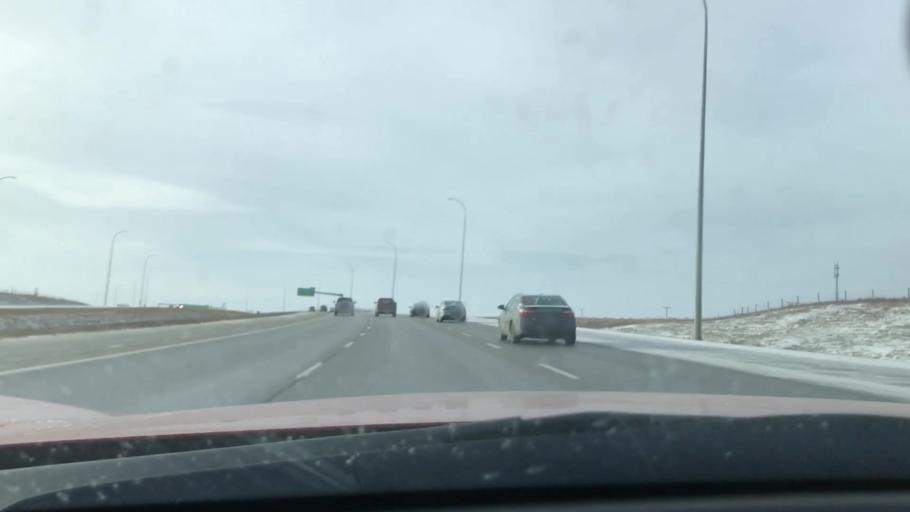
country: CA
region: Alberta
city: Calgary
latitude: 51.1508
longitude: -114.1894
